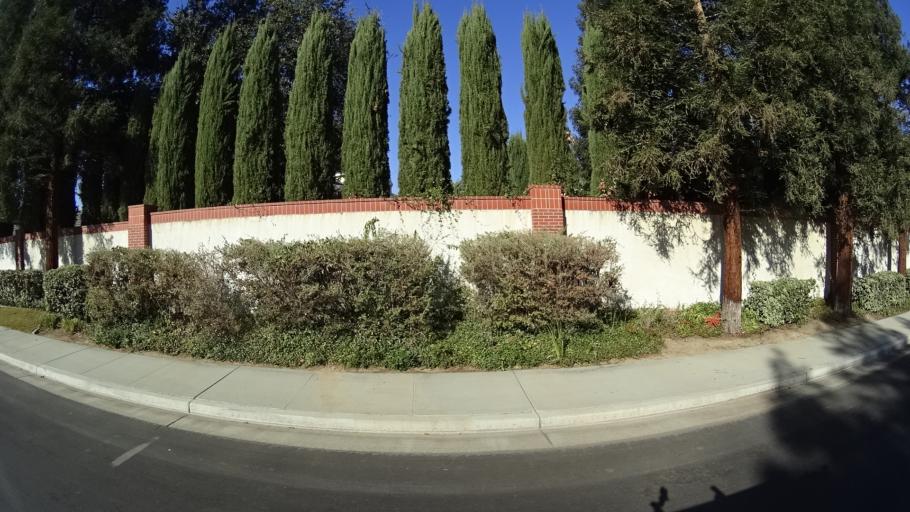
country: US
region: California
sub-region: Kern County
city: Greenacres
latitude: 35.3287
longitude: -119.1188
